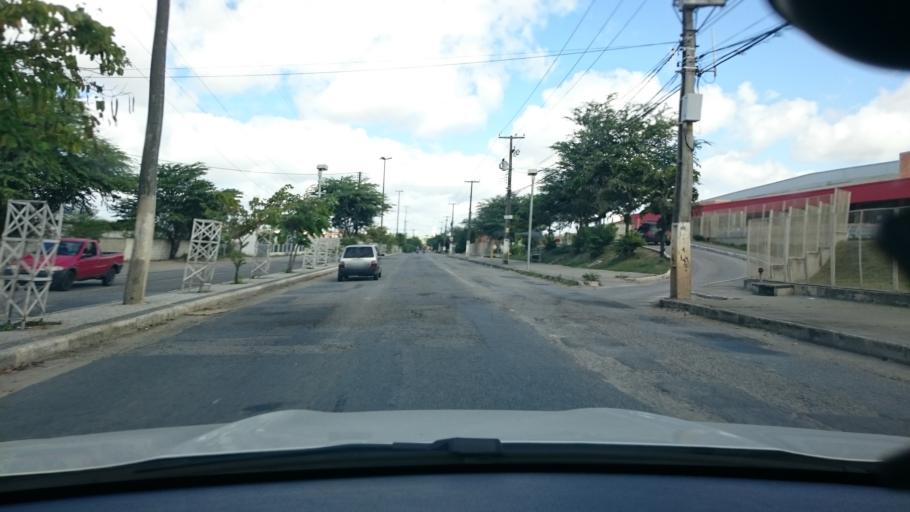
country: BR
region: Paraiba
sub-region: Campina Grande
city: Campina Grande
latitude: -7.2346
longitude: -35.9175
